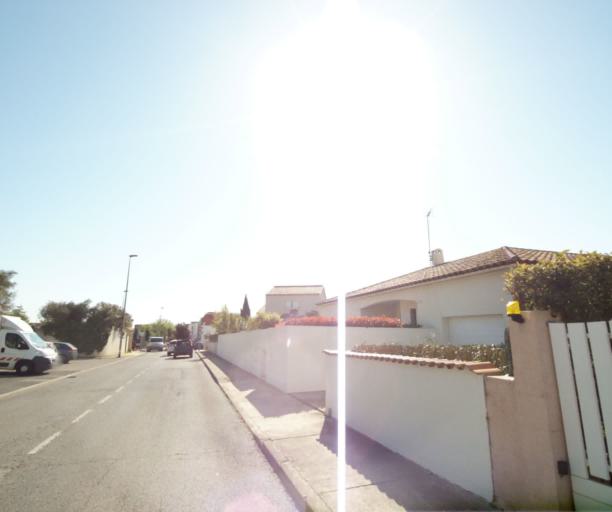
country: FR
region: Languedoc-Roussillon
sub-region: Departement de l'Herault
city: Le Cres
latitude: 43.6366
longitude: 3.9216
